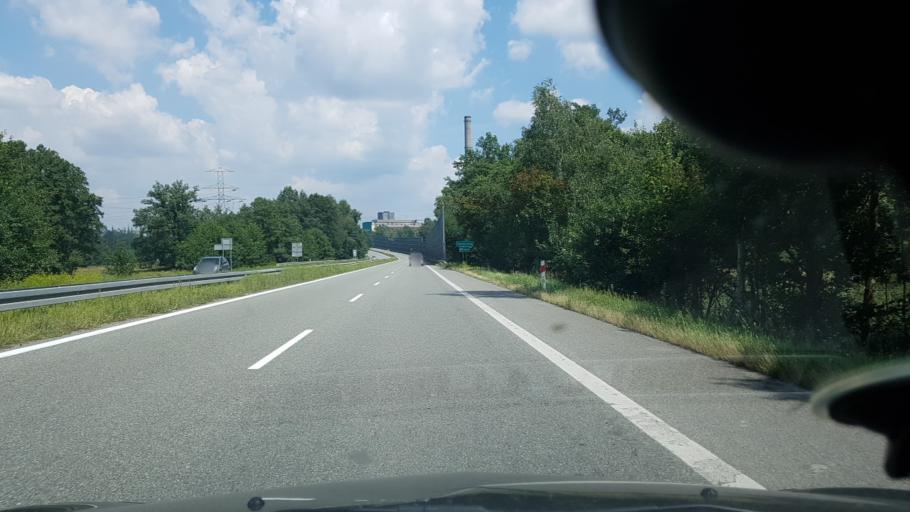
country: PL
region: Silesian Voivodeship
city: Gardawice
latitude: 50.1286
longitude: 18.8244
